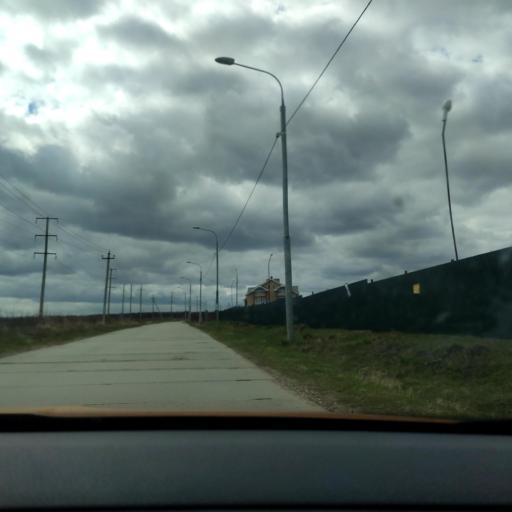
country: RU
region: Moskovskaya
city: Troitsk
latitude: 55.5070
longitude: 37.2486
